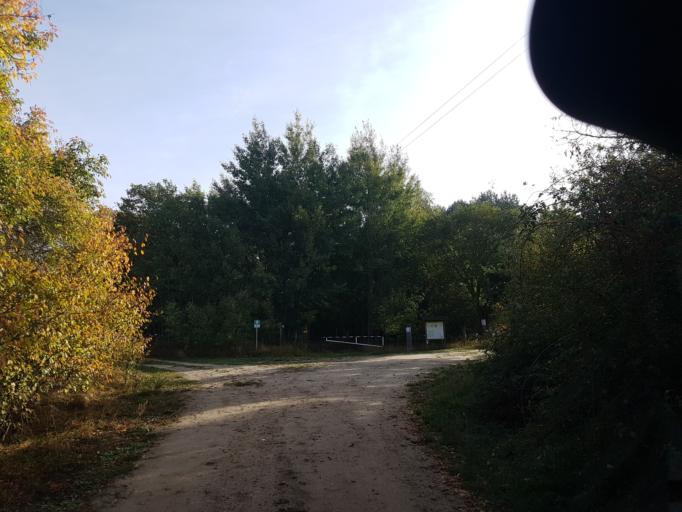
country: DE
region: Brandenburg
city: Treuenbrietzen
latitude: 52.0775
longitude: 12.9633
